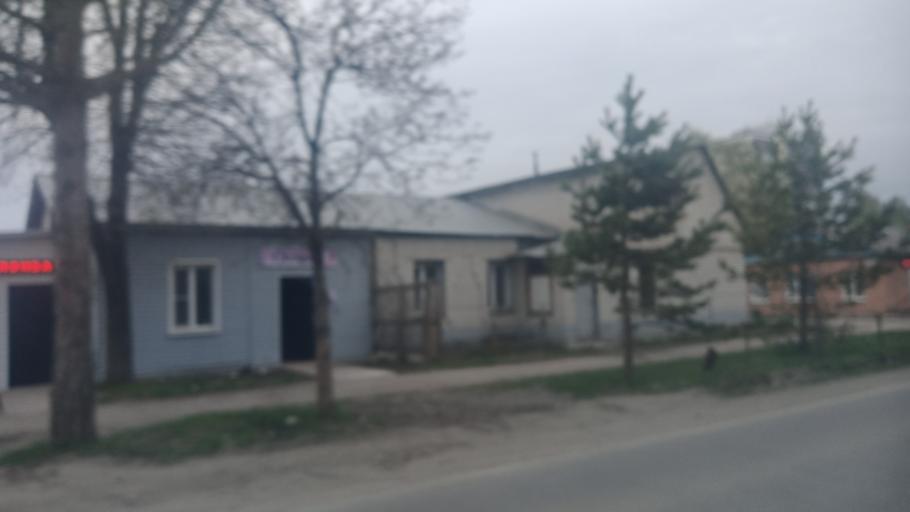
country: RU
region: Altai Krai
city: Yuzhnyy
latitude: 53.2526
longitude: 83.6861
